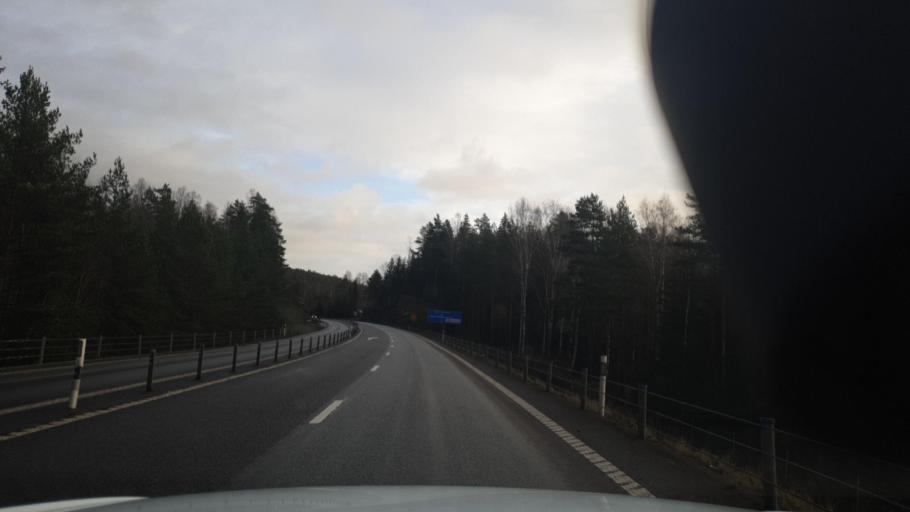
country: SE
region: Vaermland
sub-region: Arvika Kommun
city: Arvika
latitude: 59.6445
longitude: 12.7411
